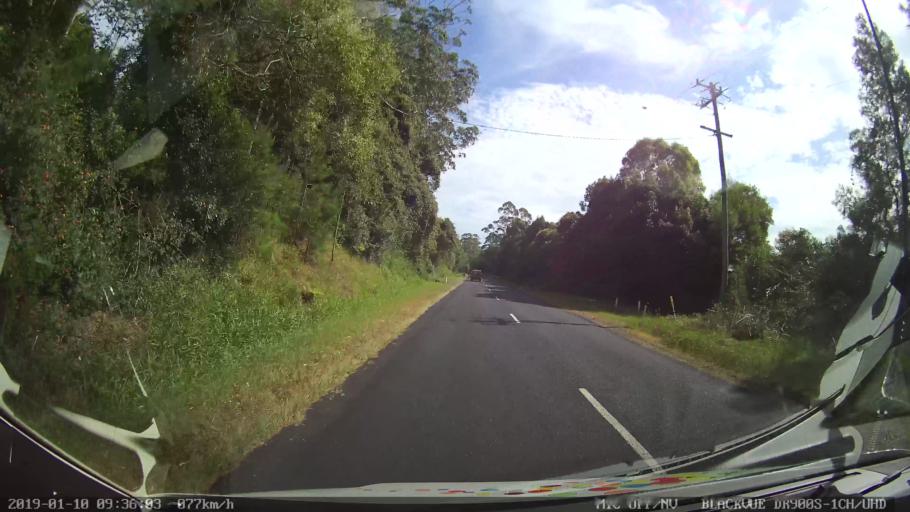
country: AU
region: New South Wales
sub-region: Coffs Harbour
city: Nana Glen
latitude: -30.2032
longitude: 153.0134
